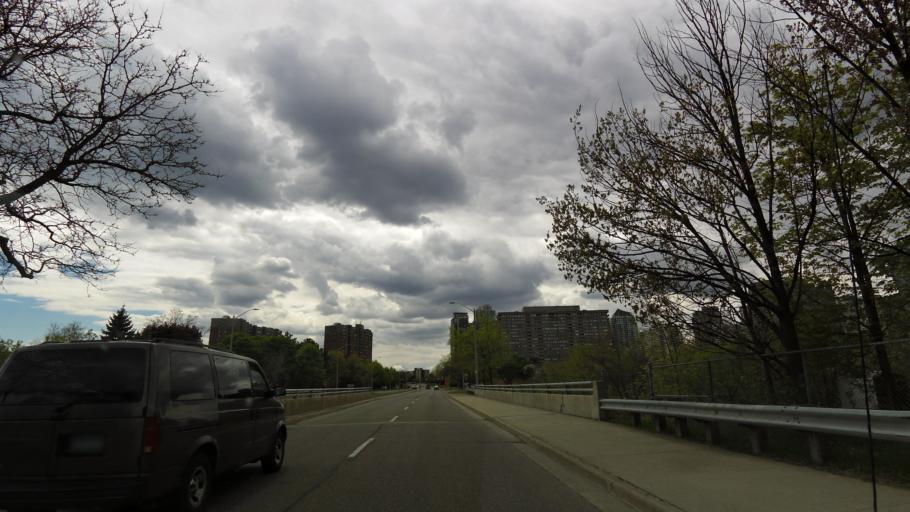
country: CA
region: Ontario
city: Mississauga
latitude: 43.5928
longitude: -79.6236
